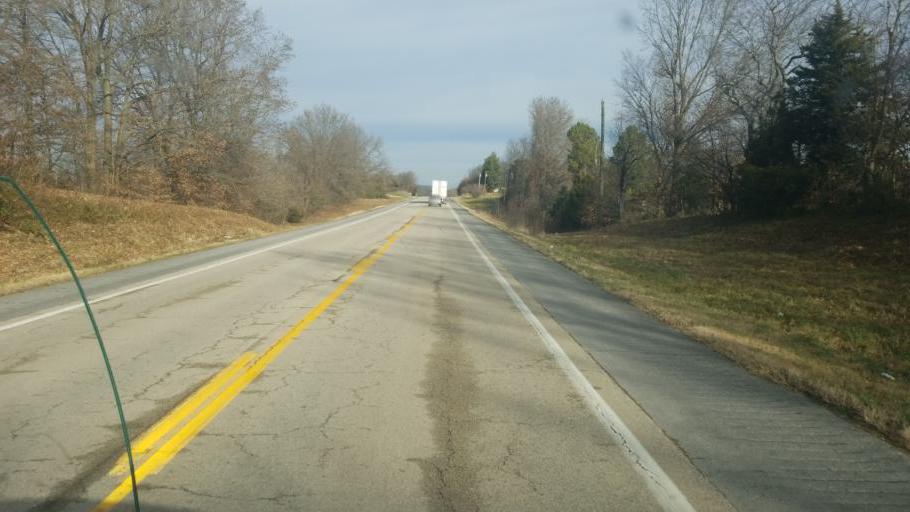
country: US
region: Missouri
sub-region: Stoddard County
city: Advance
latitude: 37.0341
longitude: -89.9040
